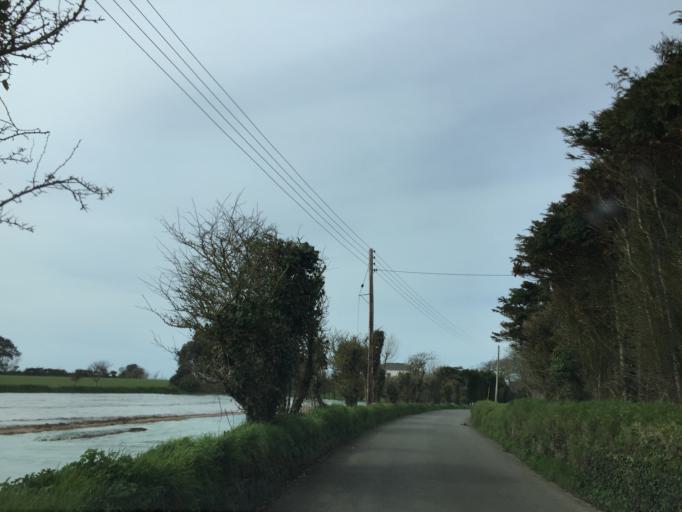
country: JE
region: St Helier
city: Saint Helier
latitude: 49.2477
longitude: -2.1673
